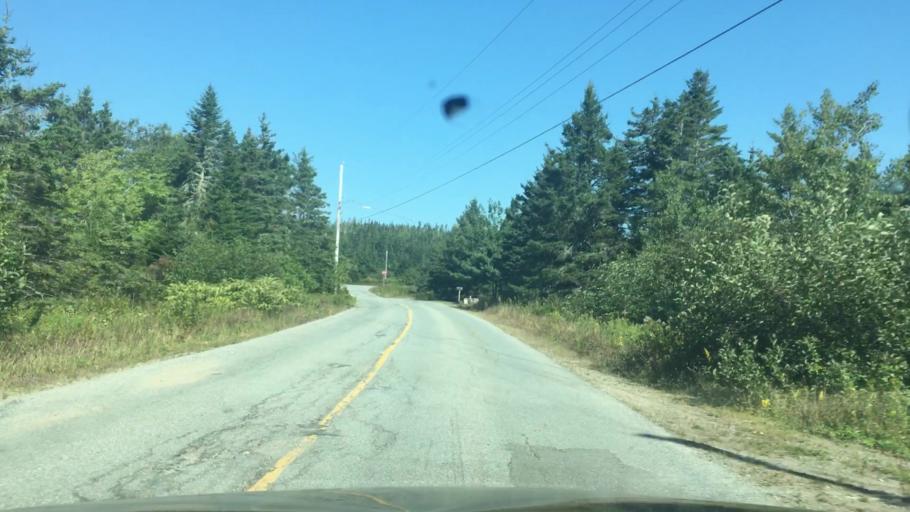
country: CA
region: Nova Scotia
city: New Glasgow
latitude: 44.8039
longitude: -62.6931
